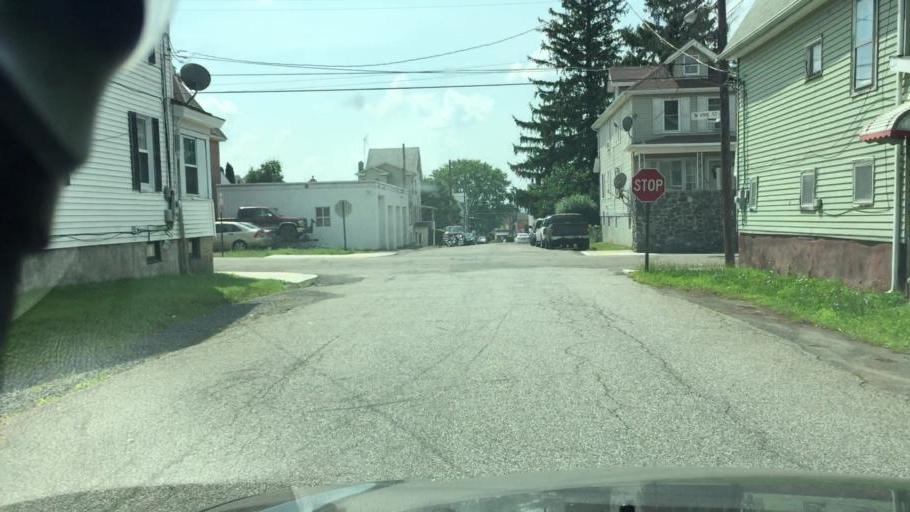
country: US
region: Pennsylvania
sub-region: Luzerne County
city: Hazleton
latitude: 40.9695
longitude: -75.9785
